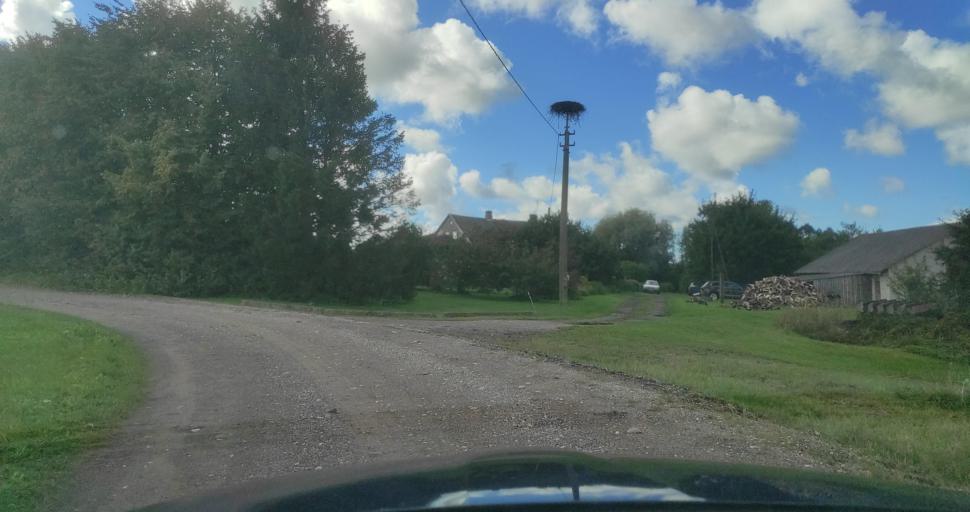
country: LV
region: Ventspils Rajons
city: Piltene
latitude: 57.2662
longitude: 21.6037
